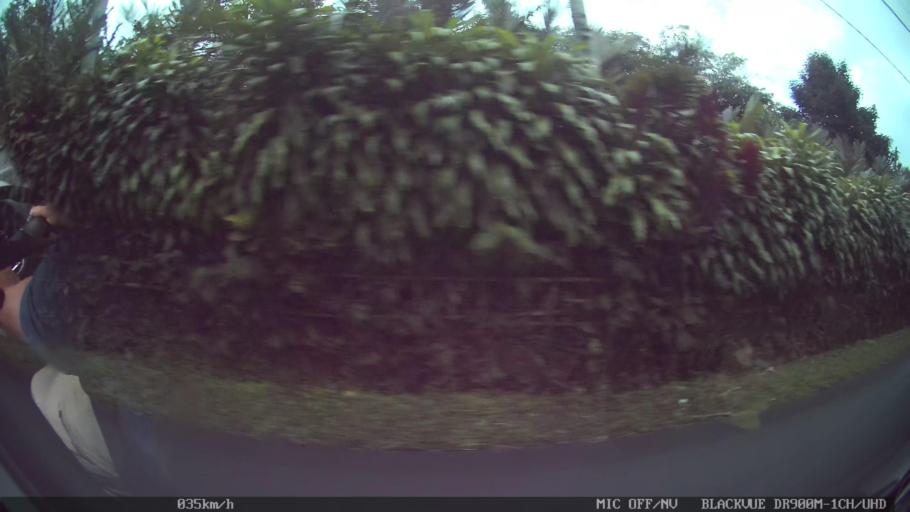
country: ID
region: Bali
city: Banjar Geriana Kangin
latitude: -8.3928
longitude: 115.4427
